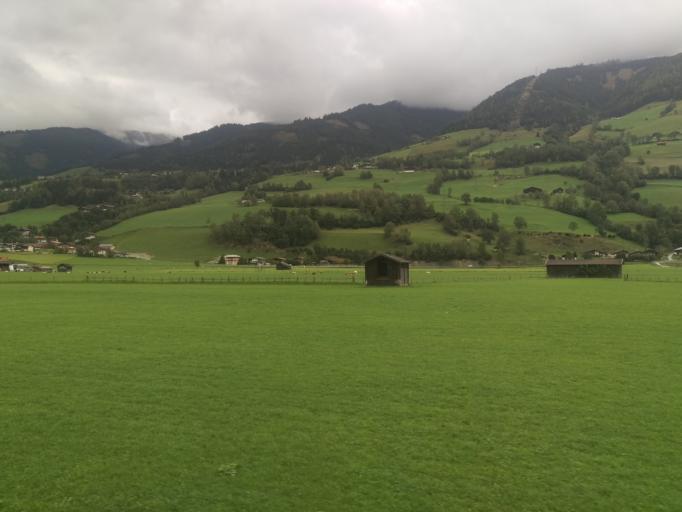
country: AT
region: Salzburg
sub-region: Politischer Bezirk Zell am See
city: Uttendorf
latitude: 47.2803
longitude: 12.5942
